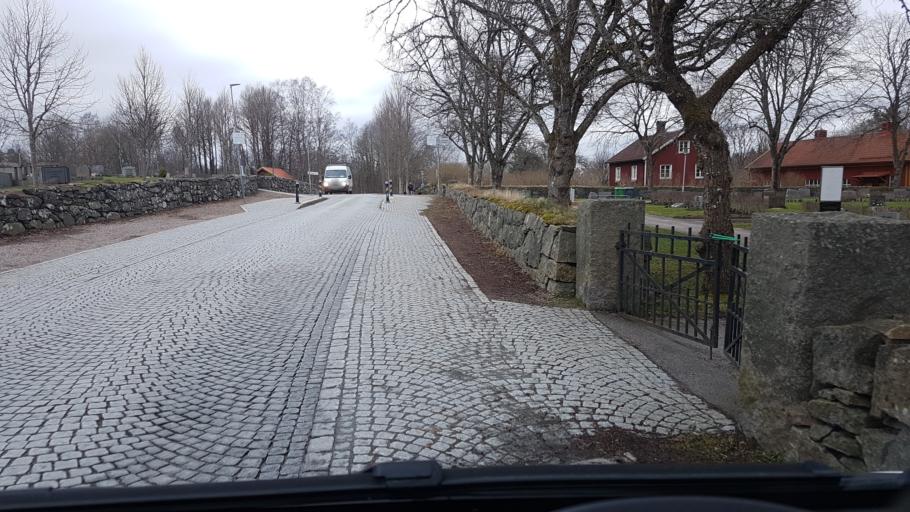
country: SE
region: Vaestra Goetaland
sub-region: Lerums Kommun
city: Stenkullen
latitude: 57.8043
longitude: 12.3803
